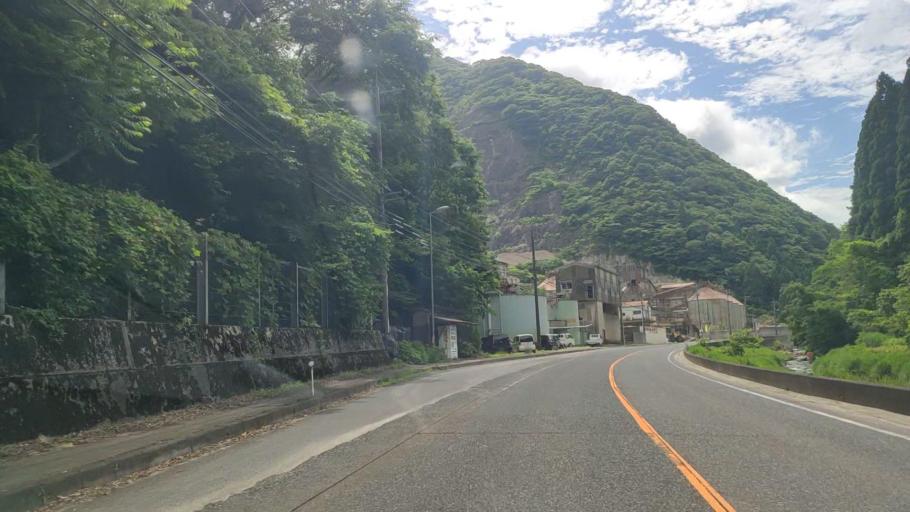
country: JP
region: Okayama
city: Niimi
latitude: 35.2223
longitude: 133.4492
